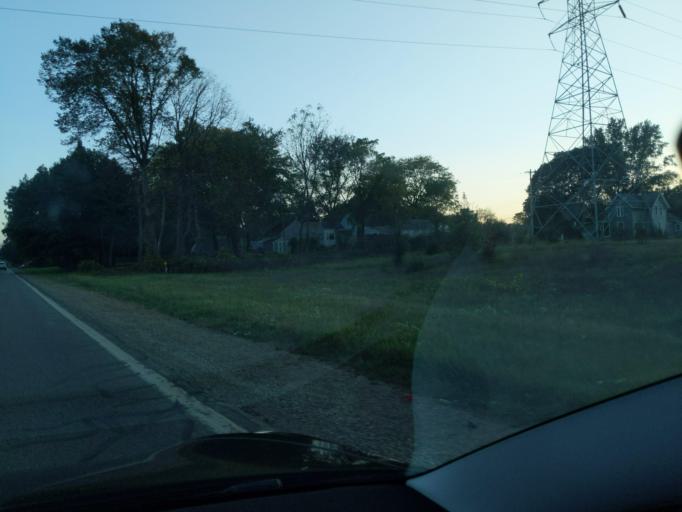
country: US
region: Michigan
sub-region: Jackson County
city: Jackson
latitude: 42.2693
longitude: -84.3844
